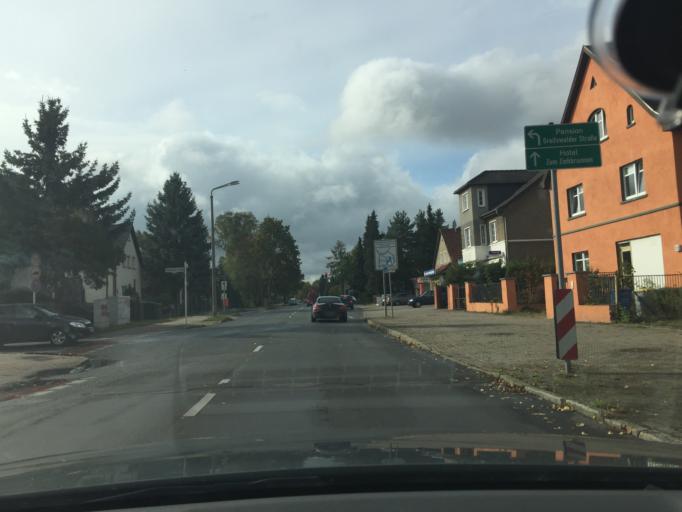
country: DE
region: Berlin
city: Hellersdorf
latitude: 52.5303
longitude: 13.6272
